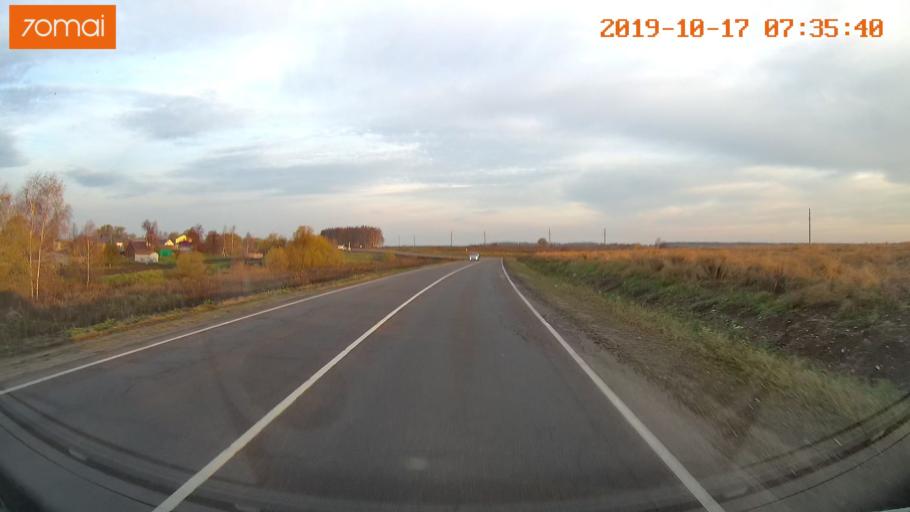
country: RU
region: Ivanovo
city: Gavrilov Posad
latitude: 56.4304
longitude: 39.9251
